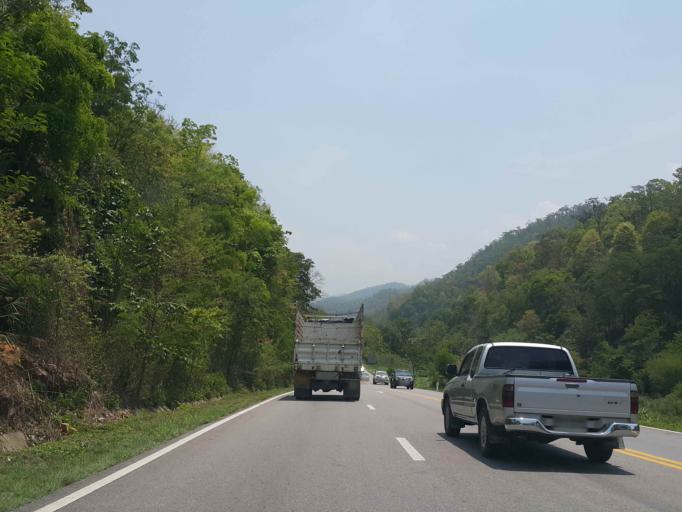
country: TH
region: Chiang Mai
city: Mae On
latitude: 18.9680
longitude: 99.2439
